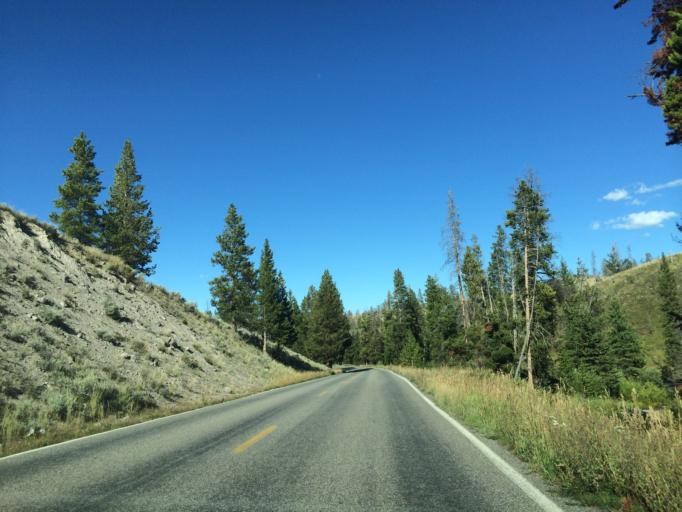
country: US
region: Montana
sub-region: Gallatin County
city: West Yellowstone
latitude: 44.8716
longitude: -110.3842
